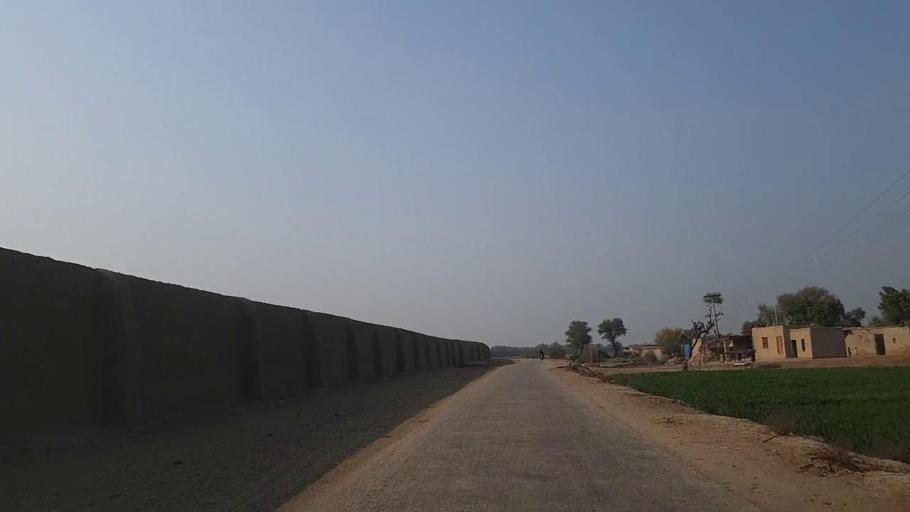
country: PK
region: Sindh
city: Sann
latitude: 26.1054
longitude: 68.1777
